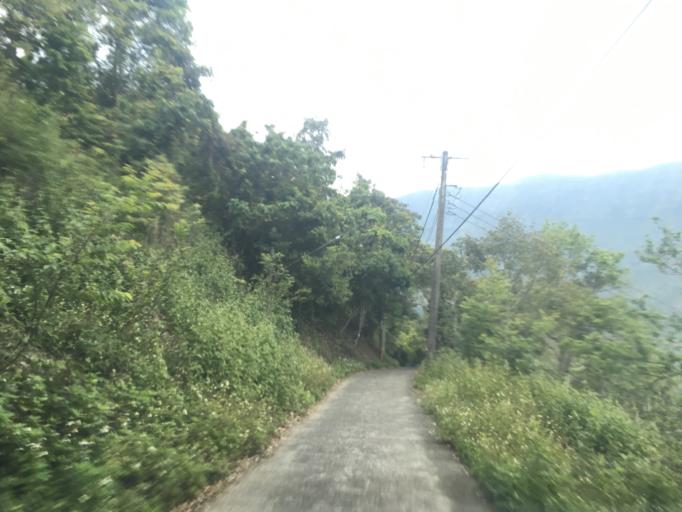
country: TW
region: Taiwan
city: Zhongxing New Village
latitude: 24.0472
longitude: 120.8029
